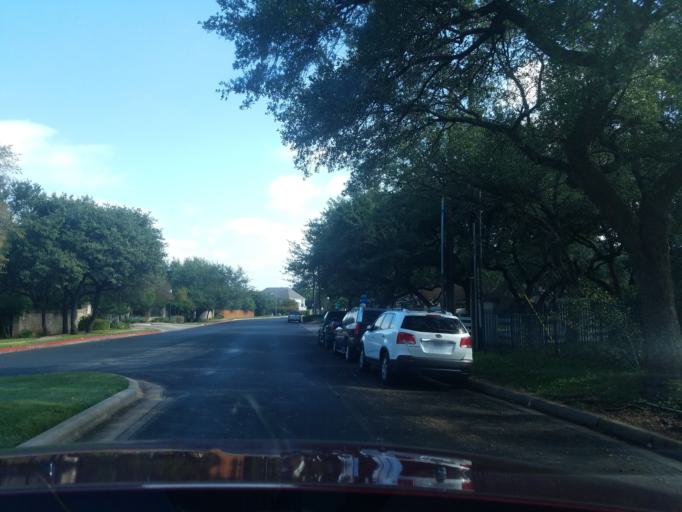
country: US
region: Texas
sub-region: Williamson County
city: Jollyville
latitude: 30.4438
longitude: -97.7754
